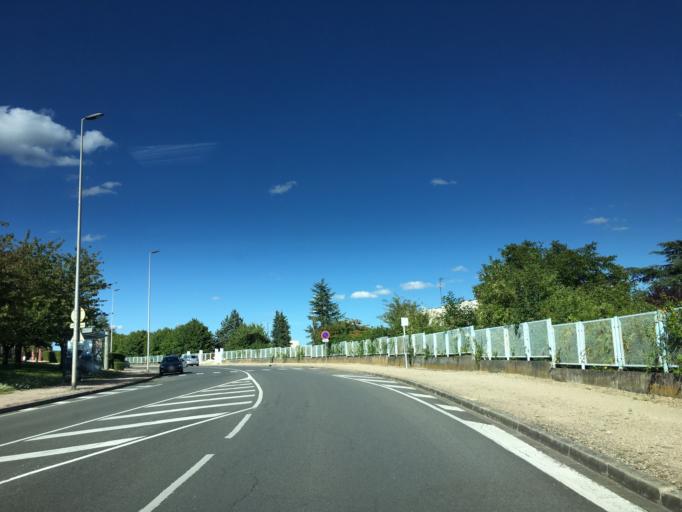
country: FR
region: Bourgogne
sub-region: Departement de l'Yonne
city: Auxerre
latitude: 47.8101
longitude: 3.5653
